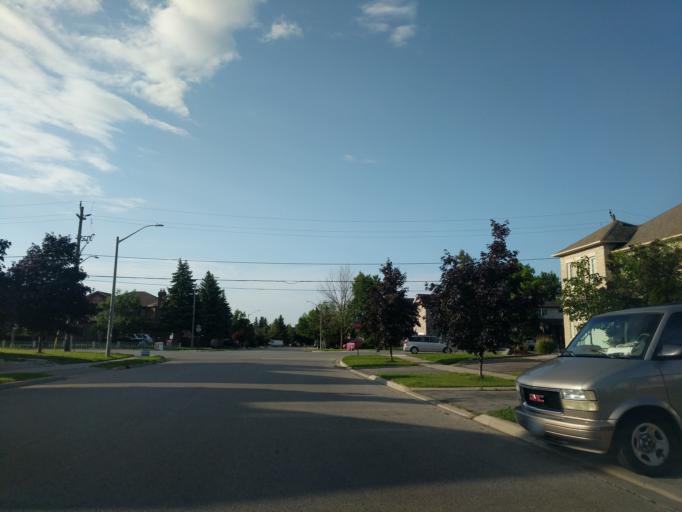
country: CA
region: Ontario
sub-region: York
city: Richmond Hill
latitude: 43.8983
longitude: -79.4473
